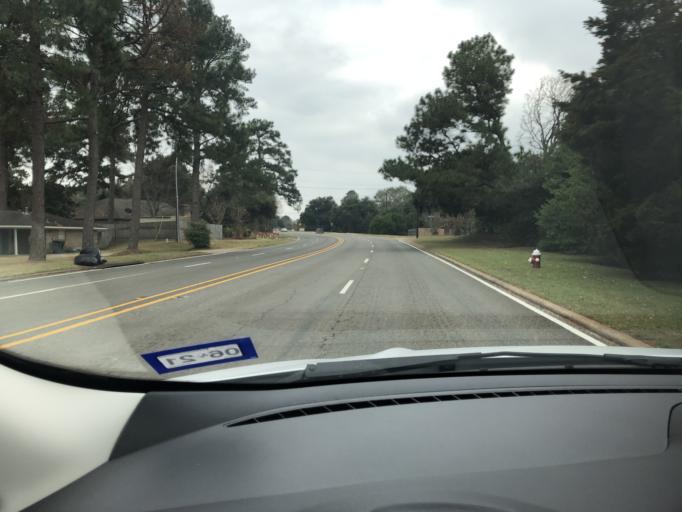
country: US
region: Texas
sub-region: Nacogdoches County
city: Nacogdoches
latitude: 31.6334
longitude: -94.6292
